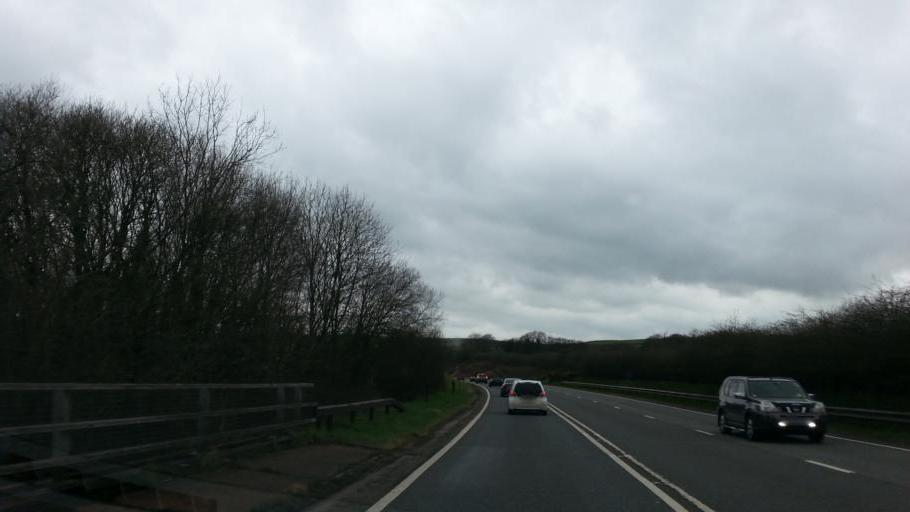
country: GB
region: England
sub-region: Devon
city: South Molton
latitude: 50.9938
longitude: -3.7119
